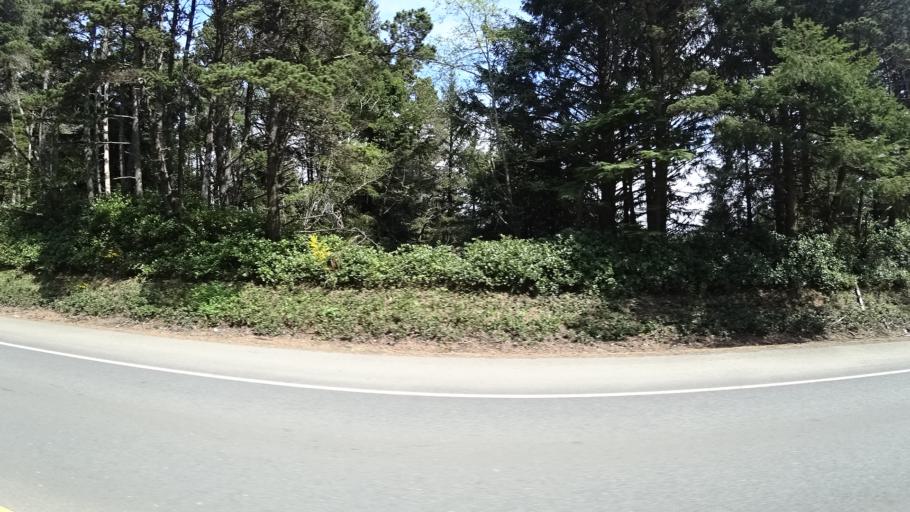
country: US
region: Oregon
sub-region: Lincoln County
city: Lincoln Beach
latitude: 44.8718
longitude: -124.0345
